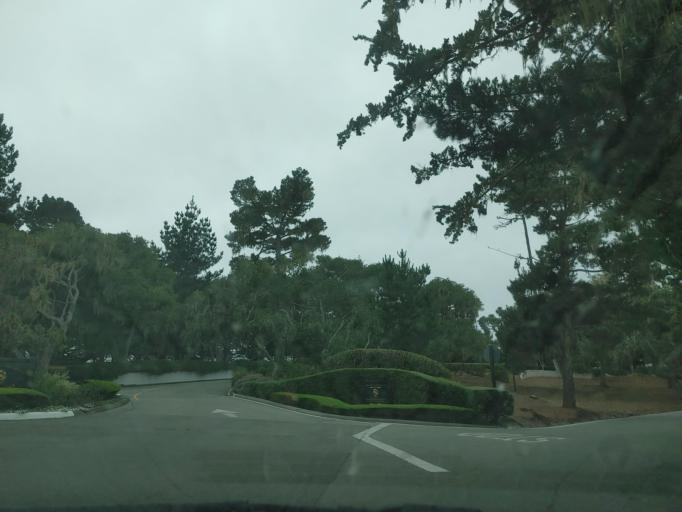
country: US
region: California
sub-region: Monterey County
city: Del Monte Forest
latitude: 36.6008
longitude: -121.9455
